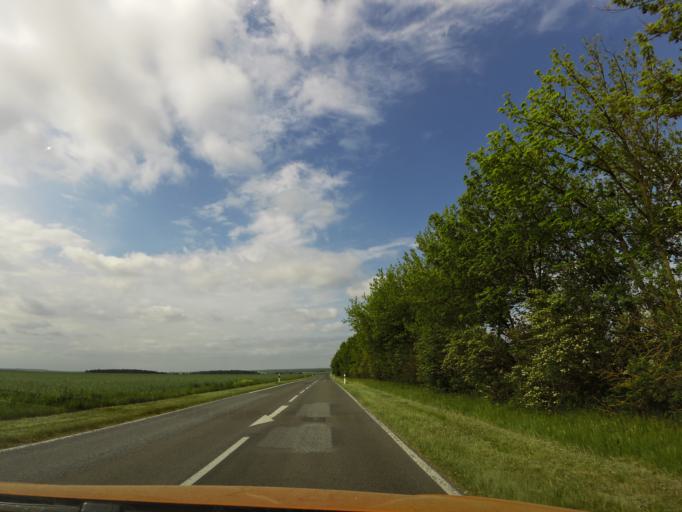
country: DE
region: Brandenburg
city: Belzig
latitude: 52.0954
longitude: 12.5531
